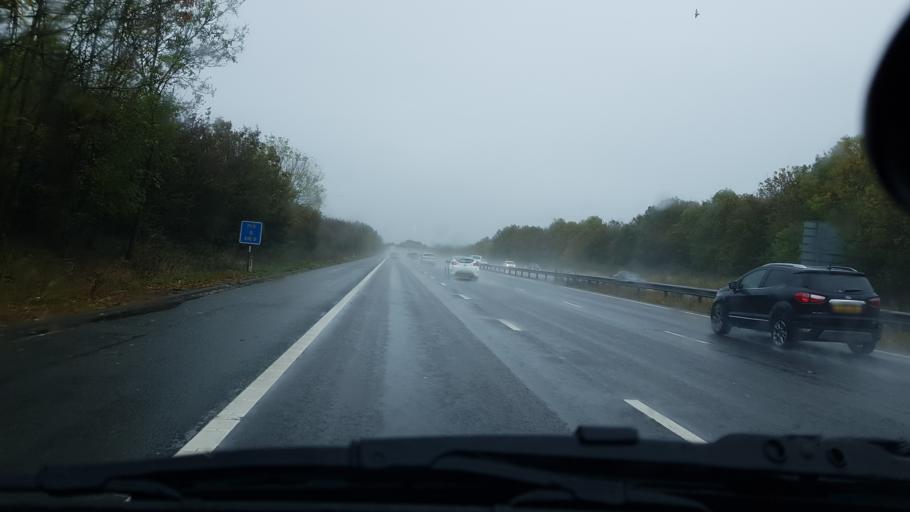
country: GB
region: England
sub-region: Worcestershire
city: Bredon
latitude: 52.0074
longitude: -2.1219
